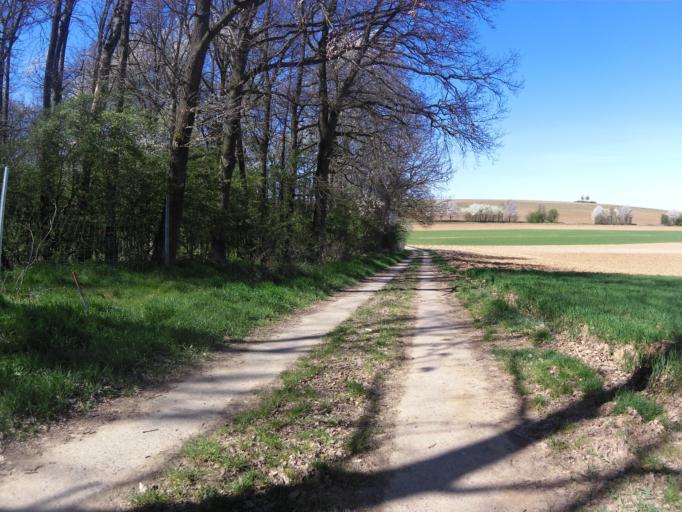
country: DE
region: Bavaria
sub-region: Regierungsbezirk Unterfranken
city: Rottendorf
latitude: 49.8100
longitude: 10.0746
